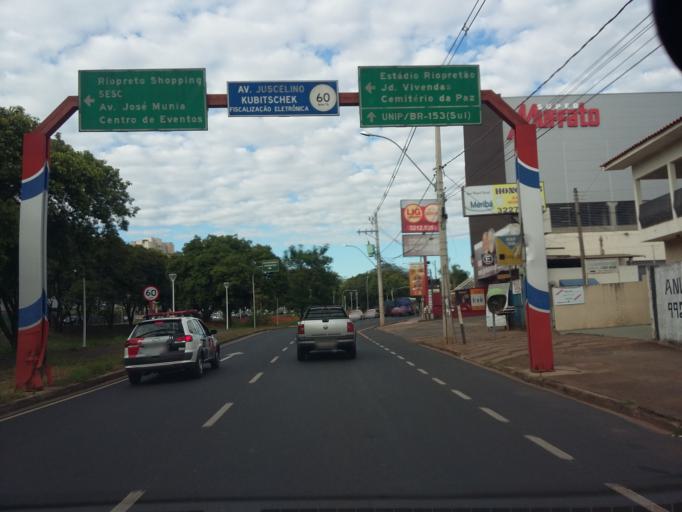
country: BR
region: Sao Paulo
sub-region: Sao Jose Do Rio Preto
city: Sao Jose do Rio Preto
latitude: -20.8295
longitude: -49.4050
